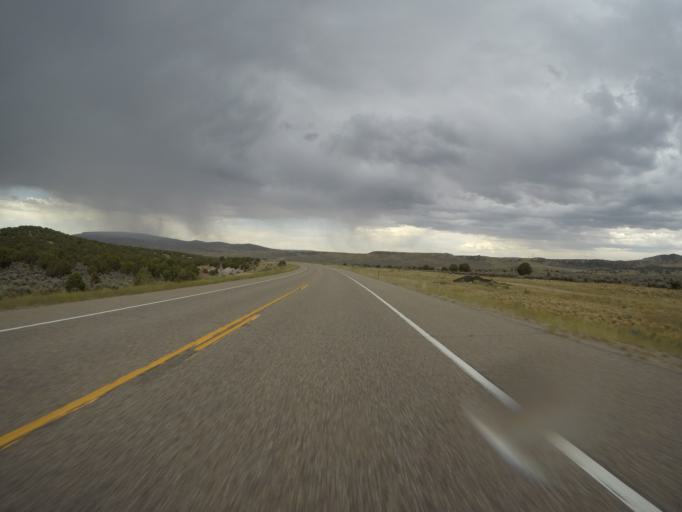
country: US
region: Colorado
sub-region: Rio Blanco County
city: Rangely
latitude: 40.3882
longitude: -108.3477
